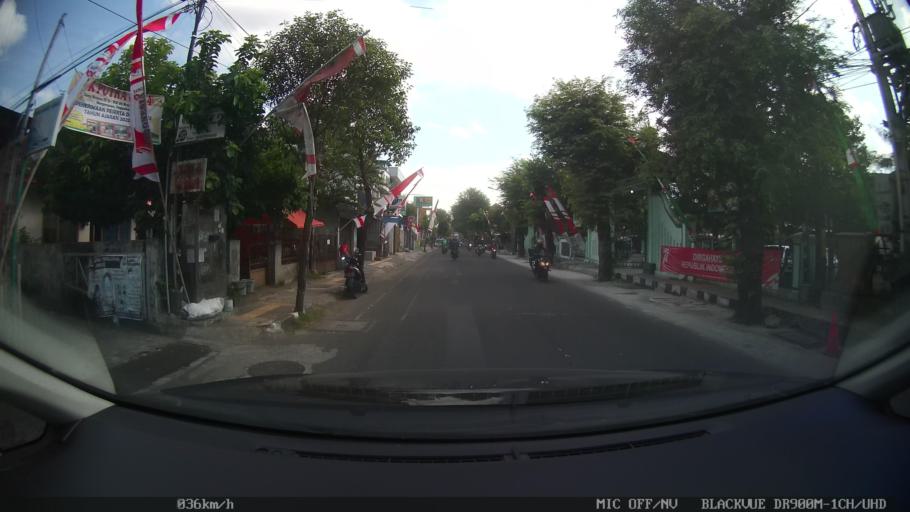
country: ID
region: Daerah Istimewa Yogyakarta
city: Yogyakarta
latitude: -7.8180
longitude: 110.3732
